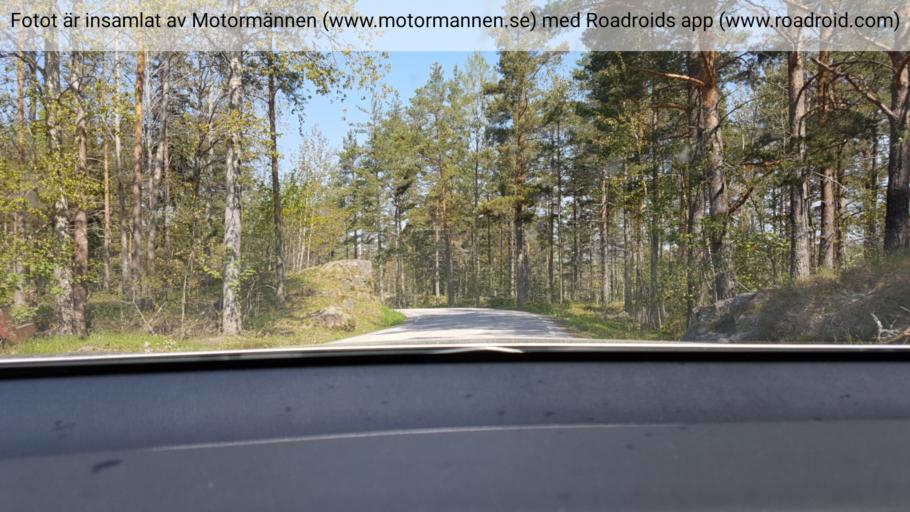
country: SE
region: Kalmar
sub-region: Vasterviks Kommun
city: Forserum
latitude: 57.8640
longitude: 16.4938
